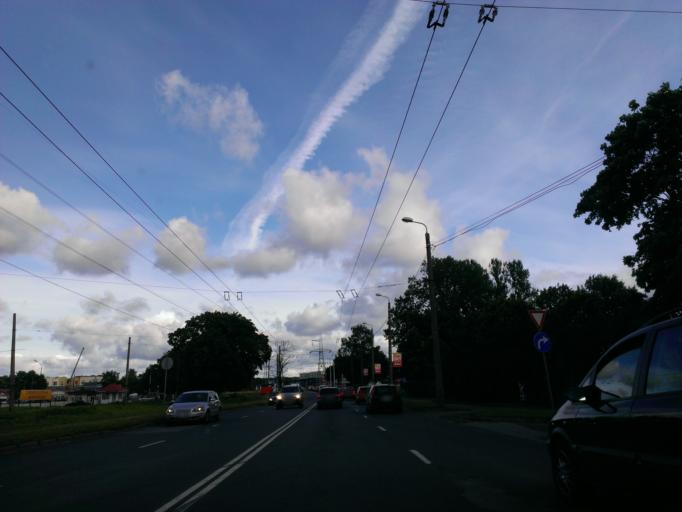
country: LV
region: Stopini
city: Ulbroka
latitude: 56.9585
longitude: 24.2342
